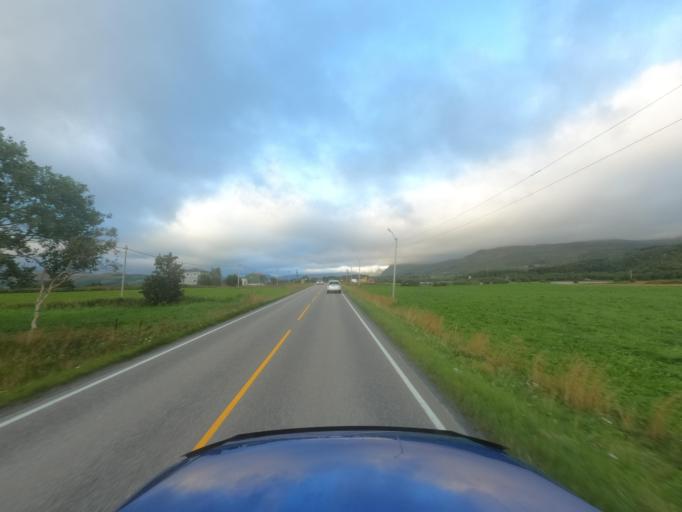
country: NO
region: Nordland
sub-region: Vestvagoy
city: Evjen
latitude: 68.2101
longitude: 13.6989
